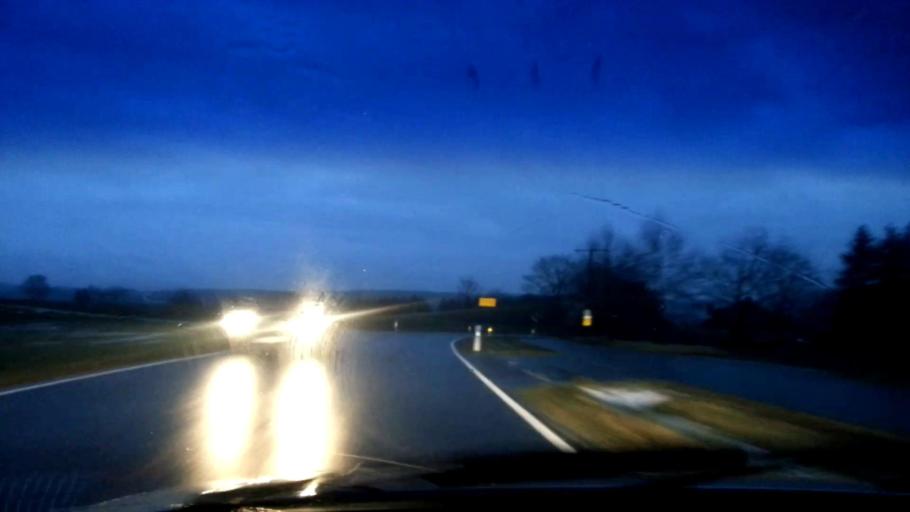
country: DE
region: Bavaria
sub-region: Upper Franconia
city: Memmelsdorf
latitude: 49.9461
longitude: 10.9559
